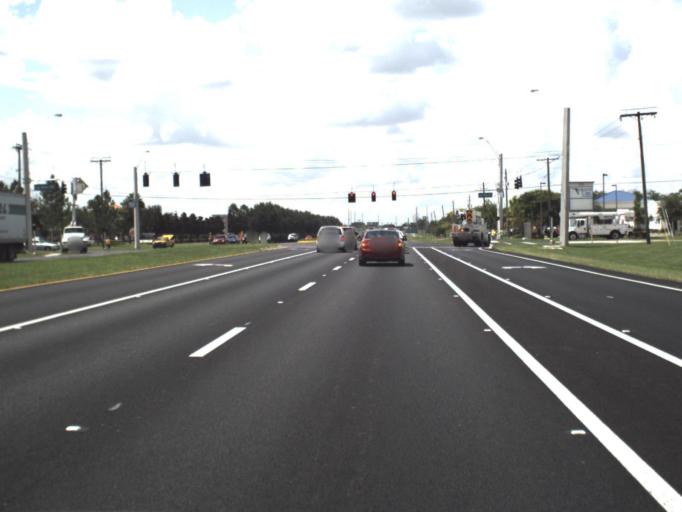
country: US
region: Florida
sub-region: Polk County
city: Cypress Gardens
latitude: 27.9786
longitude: -81.6514
